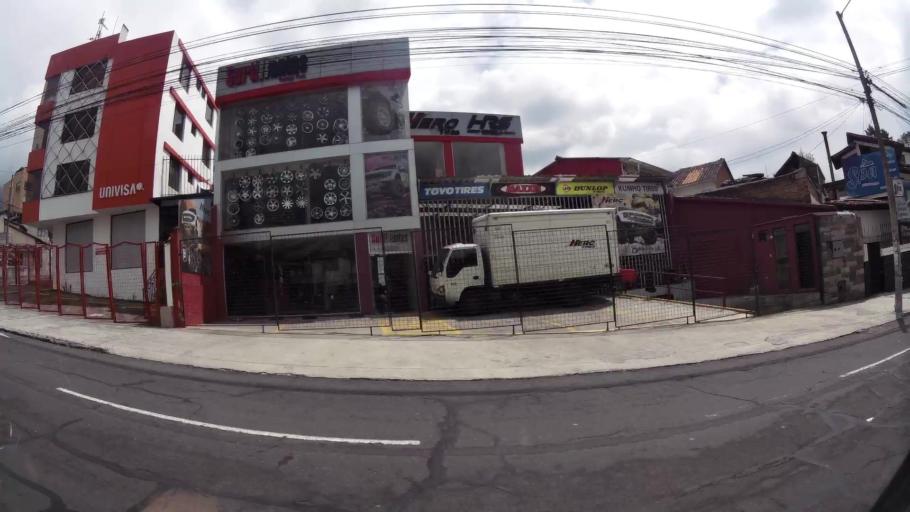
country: EC
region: Pichincha
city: Quito
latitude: -0.1851
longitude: -78.4933
